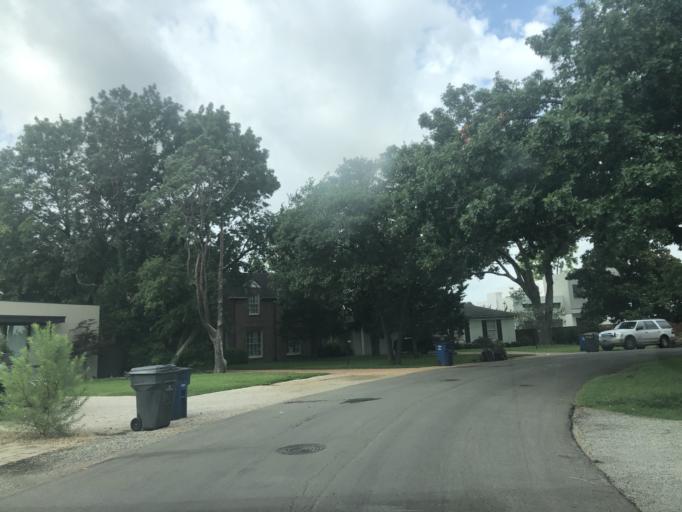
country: US
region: Texas
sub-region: Dallas County
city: University Park
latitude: 32.8573
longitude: -96.8234
